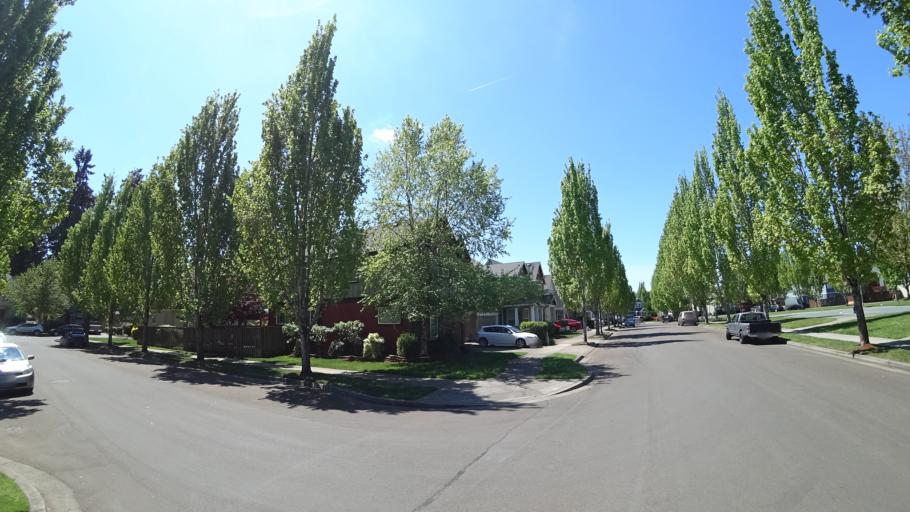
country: US
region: Oregon
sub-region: Washington County
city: Hillsboro
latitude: 45.5080
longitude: -122.9740
